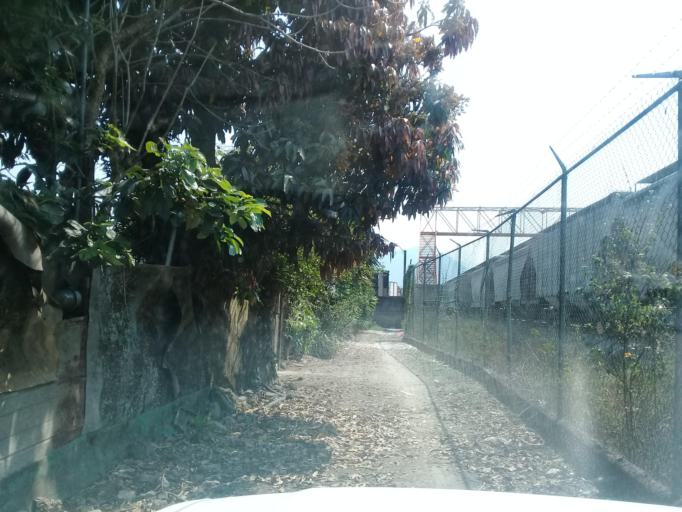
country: MX
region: Veracruz
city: Ixtac Zoquitlan
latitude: 18.8724
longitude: -97.0591
